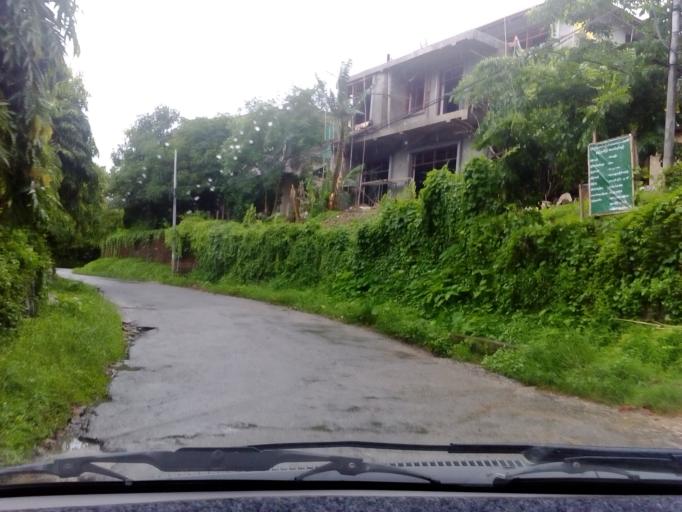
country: MM
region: Yangon
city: Yangon
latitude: 16.8151
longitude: 96.1486
